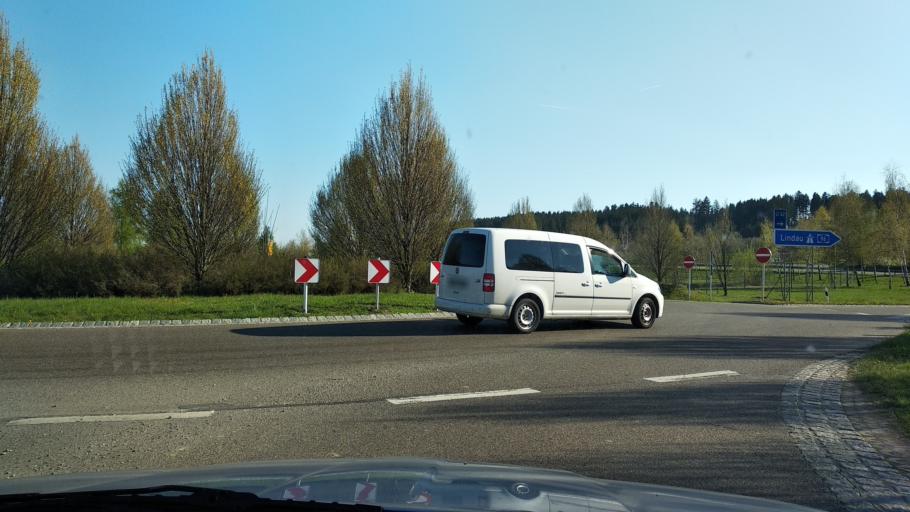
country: DE
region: Bavaria
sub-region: Swabia
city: Westerheim
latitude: 48.0294
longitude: 10.3245
